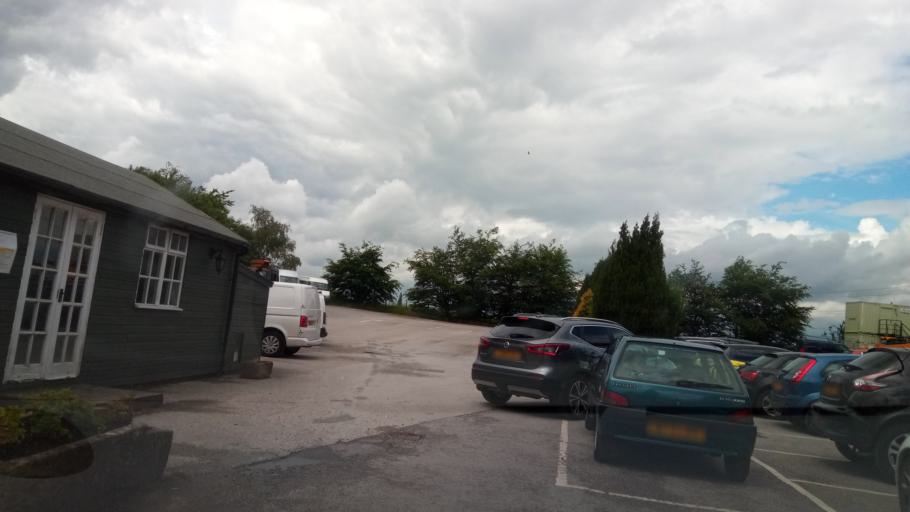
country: GB
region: England
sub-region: Derbyshire
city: Melbourne
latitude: 52.8510
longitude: -1.4023
